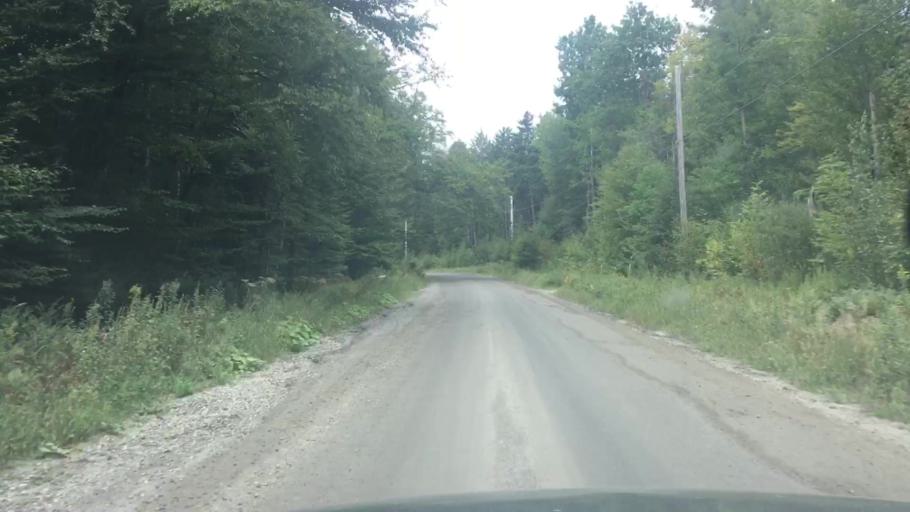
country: US
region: Vermont
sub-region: Windham County
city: Dover
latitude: 42.8245
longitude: -72.7837
